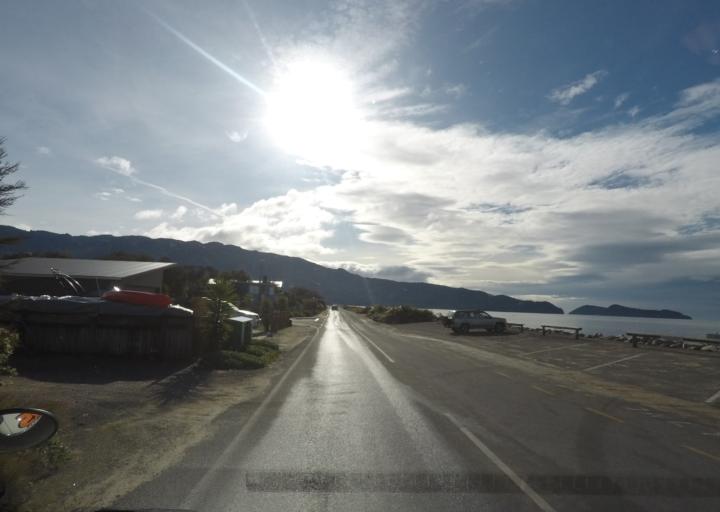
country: NZ
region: Tasman
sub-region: Tasman District
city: Motueka
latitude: -41.0079
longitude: 173.0089
